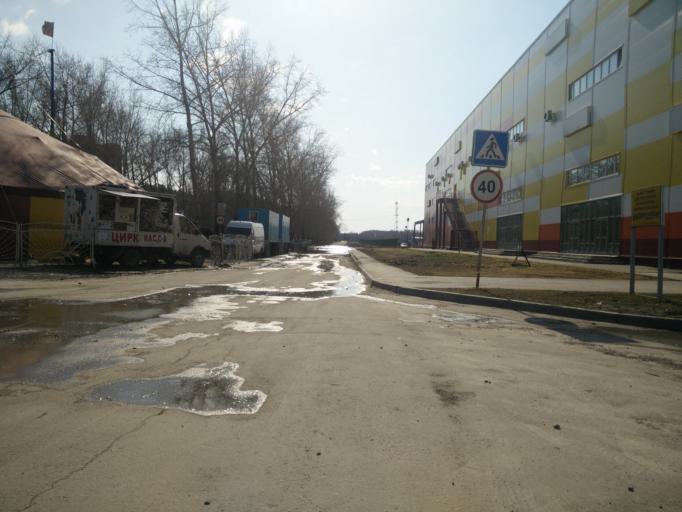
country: RU
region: Novosibirsk
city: Berdsk
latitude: 54.7651
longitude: 83.0819
